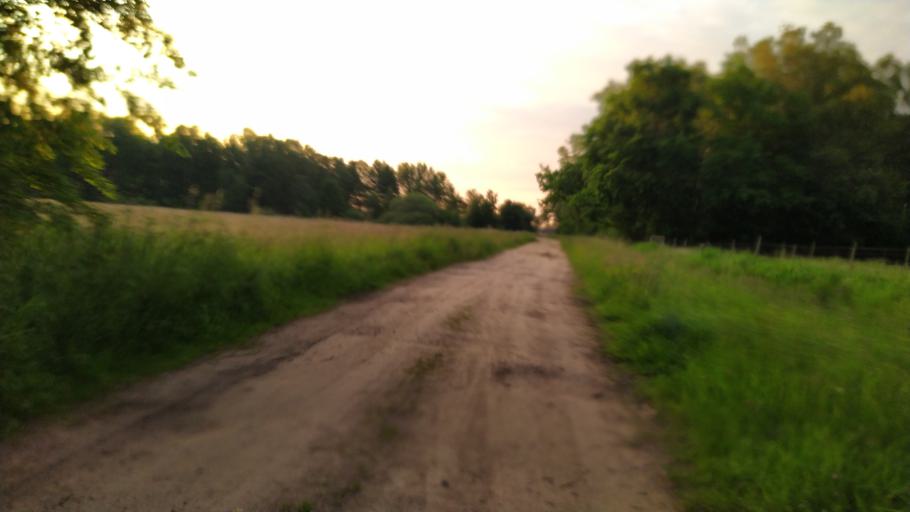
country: DE
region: Lower Saxony
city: Neu Wulmstorf
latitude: 53.4885
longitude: 9.8265
